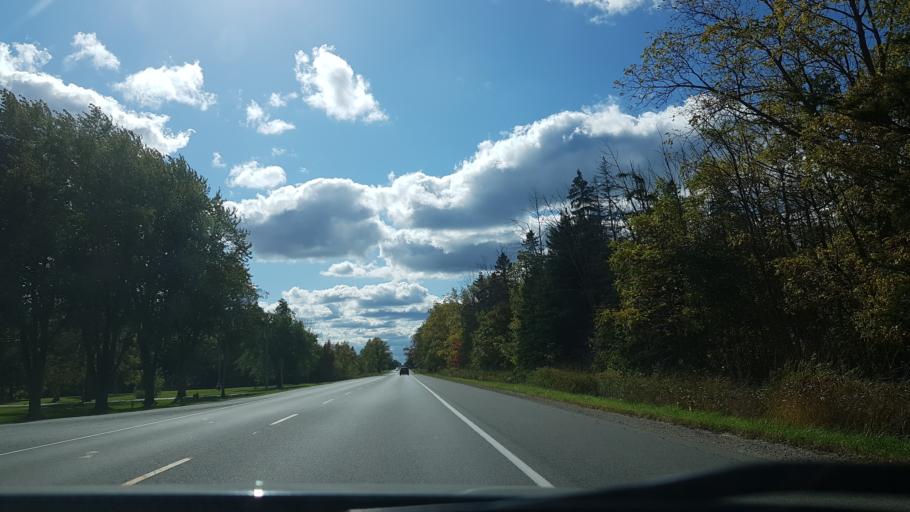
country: CA
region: Ontario
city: Bluewater
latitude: 43.3274
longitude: -81.7445
